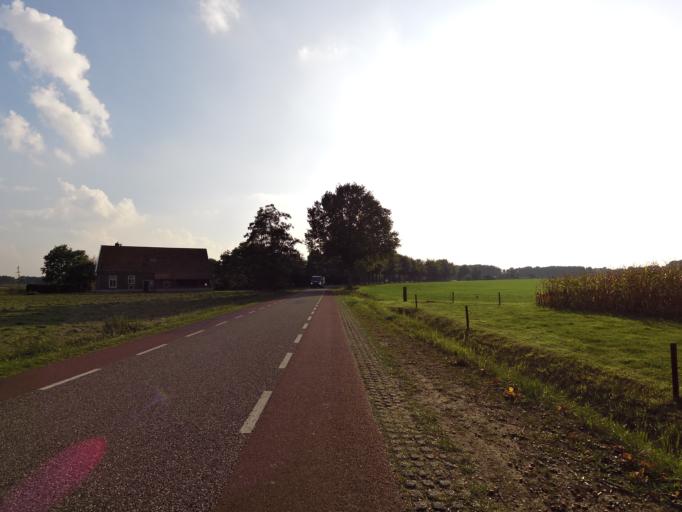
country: NL
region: Gelderland
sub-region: Gemeente Aalten
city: Aalten
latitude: 51.9079
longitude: 6.5191
